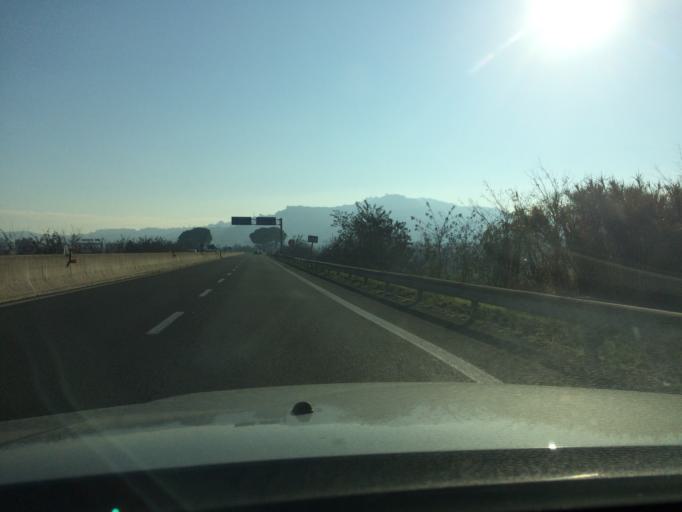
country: IT
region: Umbria
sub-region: Provincia di Perugia
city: Ponterio-Pian di Porto
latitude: 42.8075
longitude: 12.4068
